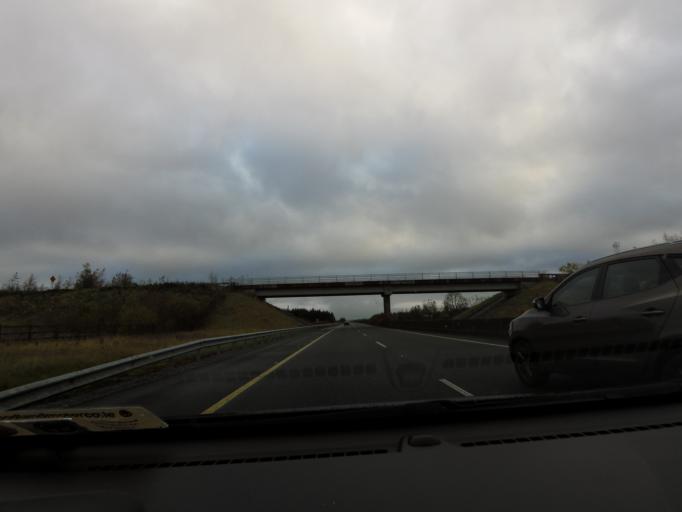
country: IE
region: Connaught
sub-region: County Galway
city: Ballinasloe
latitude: 53.2908
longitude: -8.3771
